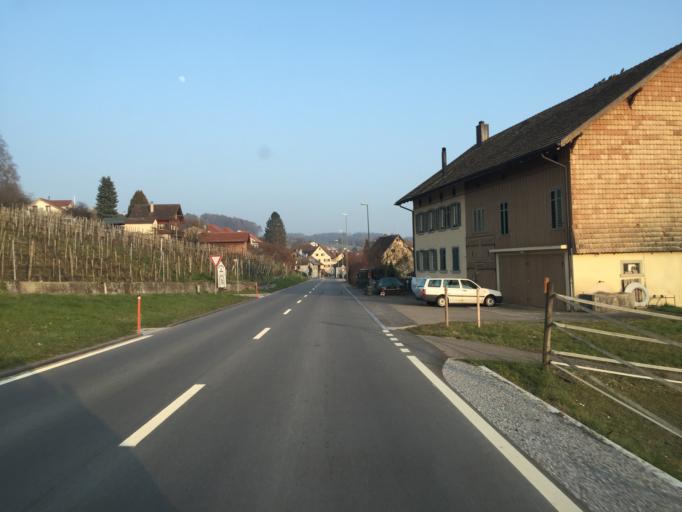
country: CH
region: Zurich
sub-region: Bezirk Andelfingen
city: Uhwiesen
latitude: 47.6546
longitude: 8.6489
